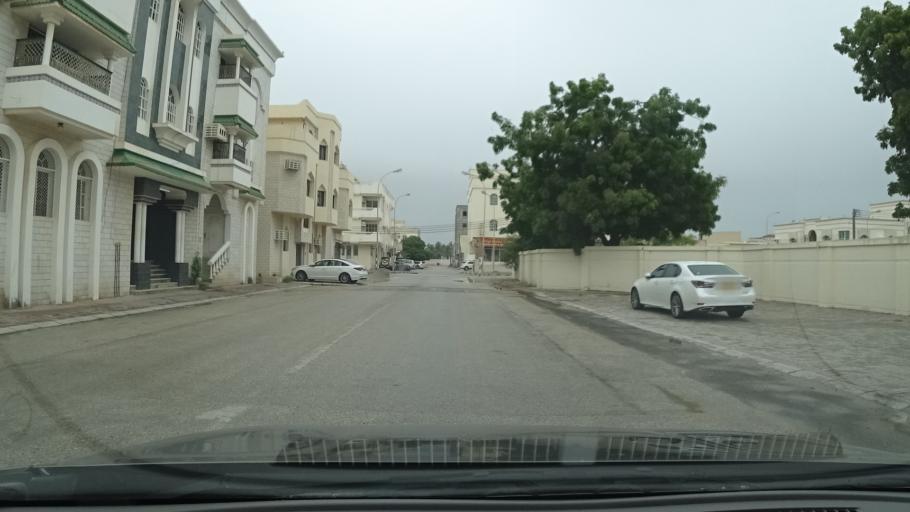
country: OM
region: Zufar
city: Salalah
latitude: 17.0247
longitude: 54.1583
